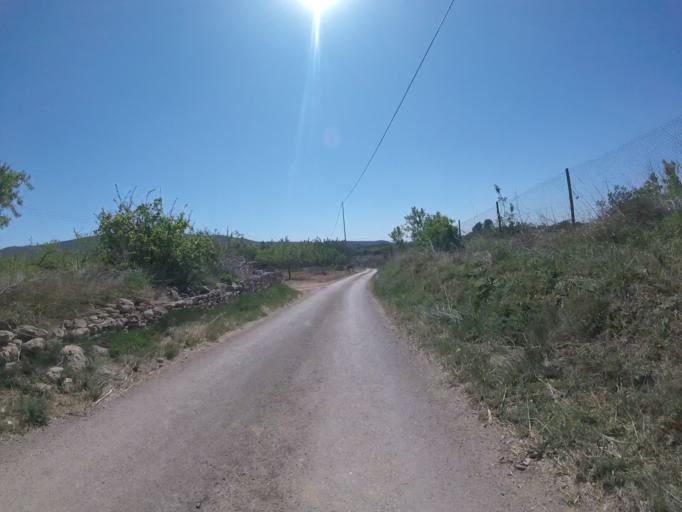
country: ES
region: Valencia
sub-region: Provincia de Castello
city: Cuevas de Vinroma
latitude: 40.3755
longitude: 0.1340
